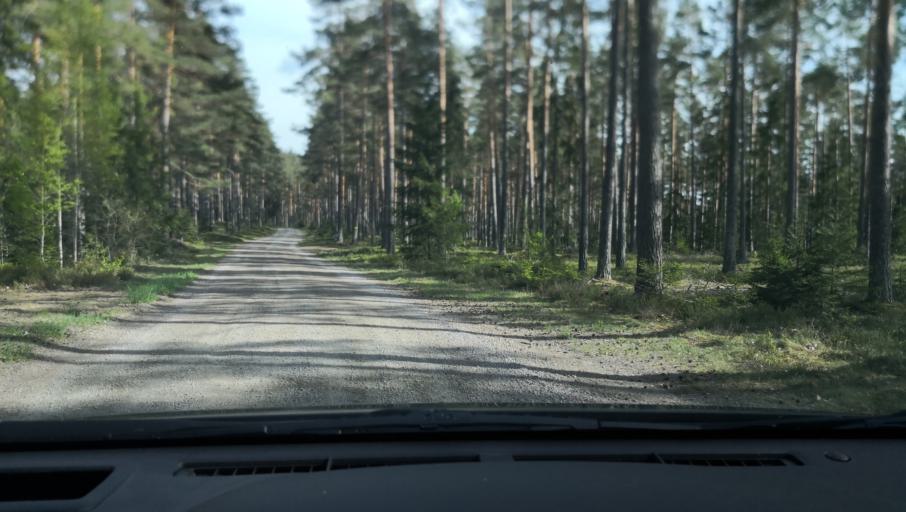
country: SE
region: OErebro
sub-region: Askersunds Kommun
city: Asbro
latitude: 59.0356
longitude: 15.0399
